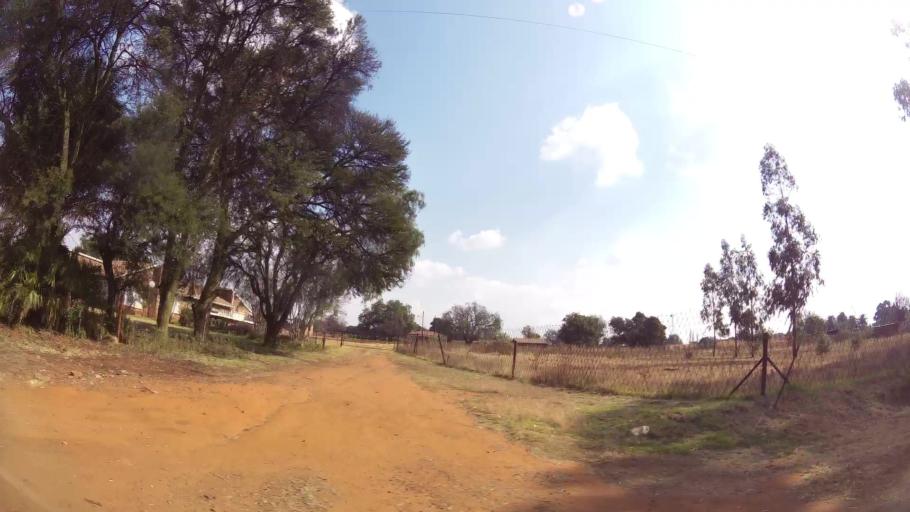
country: ZA
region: Mpumalanga
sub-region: Nkangala District Municipality
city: Delmas
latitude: -26.1753
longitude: 28.5408
